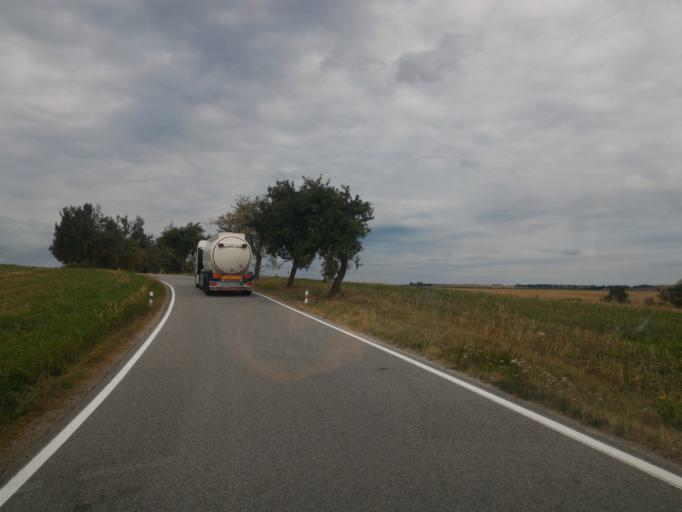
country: CZ
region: Vysocina
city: Zeletava
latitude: 49.1608
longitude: 15.5824
